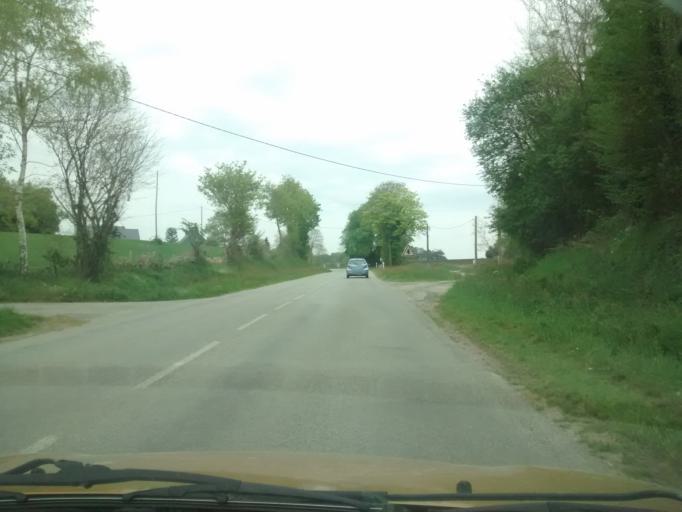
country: FR
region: Brittany
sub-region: Departement du Morbihan
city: Questembert
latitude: 47.6516
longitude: -2.4855
